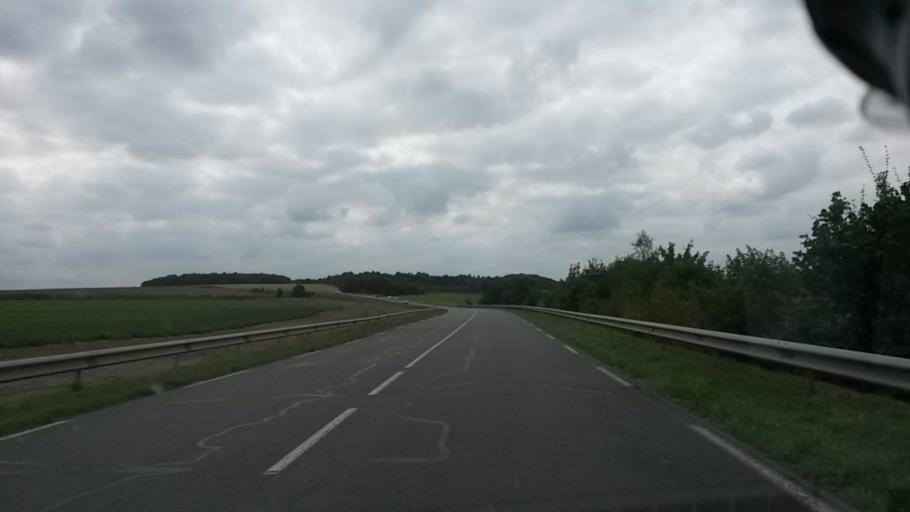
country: FR
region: Picardie
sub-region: Departement de la Somme
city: Camon
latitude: 49.9430
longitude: 2.4188
